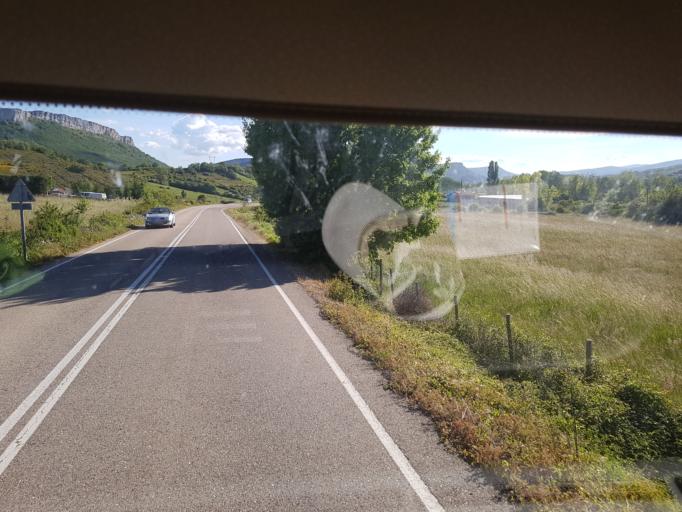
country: ES
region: Castille and Leon
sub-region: Provincia de Burgos
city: Espinosa de los Monteros
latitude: 43.0682
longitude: -3.5665
